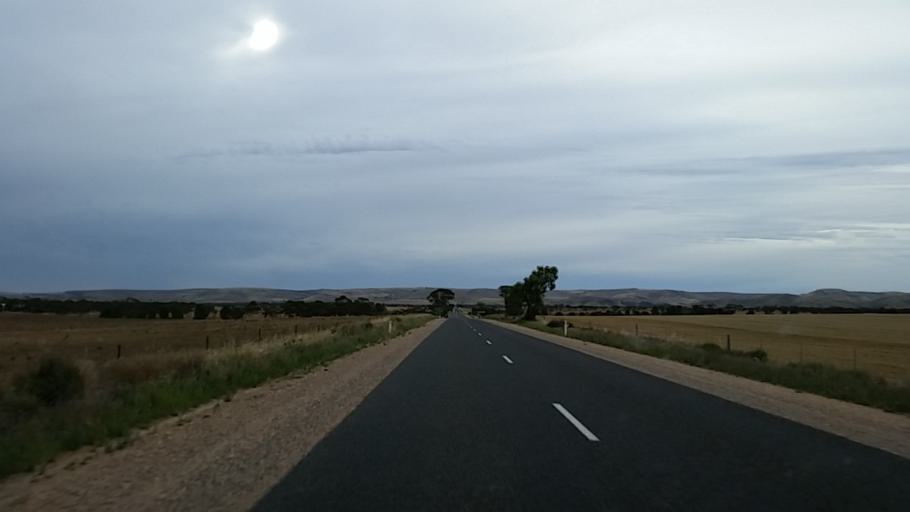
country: AU
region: South Australia
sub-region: Mid Murray
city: Mannum
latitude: -34.7554
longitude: 139.2688
